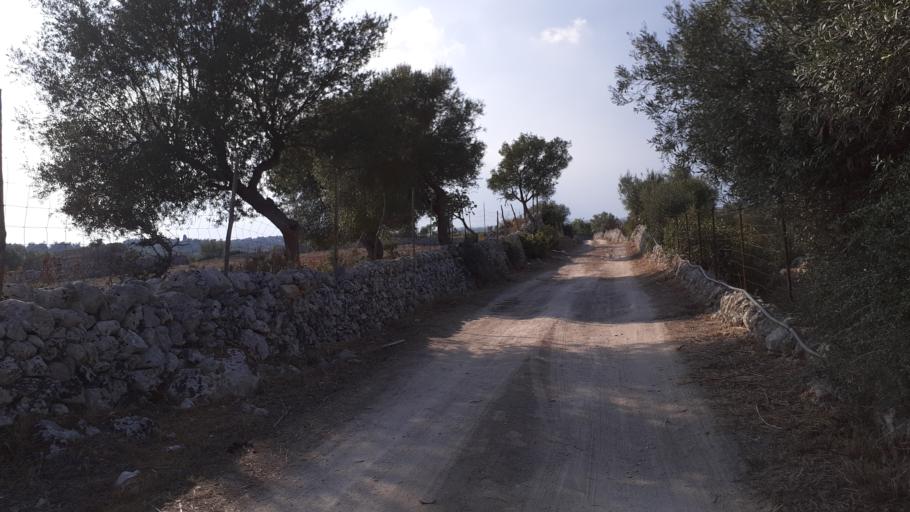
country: IT
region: Sicily
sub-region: Provincia di Siracusa
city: Canicattini Bagni
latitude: 36.9801
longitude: 15.0932
